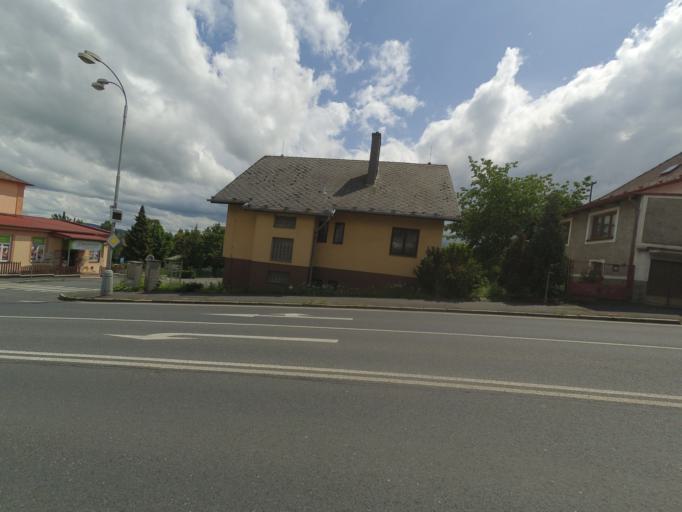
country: CZ
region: Plzensky
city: Klatovy
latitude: 49.3937
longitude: 13.2809
